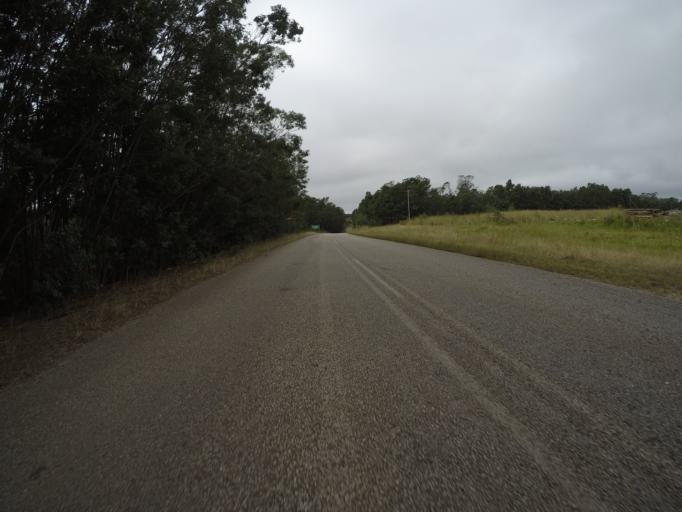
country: ZA
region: Eastern Cape
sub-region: Cacadu District Municipality
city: Kareedouw
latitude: -33.9811
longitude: 24.0475
